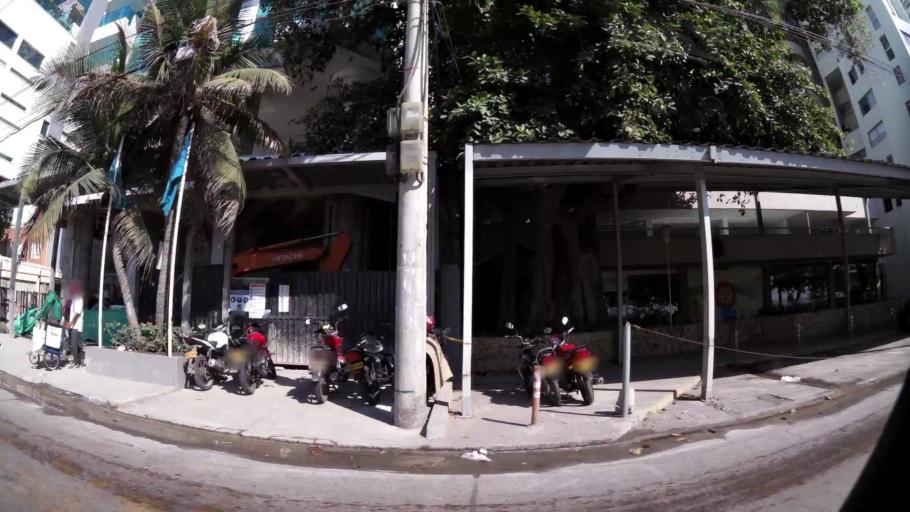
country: CO
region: Bolivar
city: Cartagena
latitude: 10.4091
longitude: -75.5517
